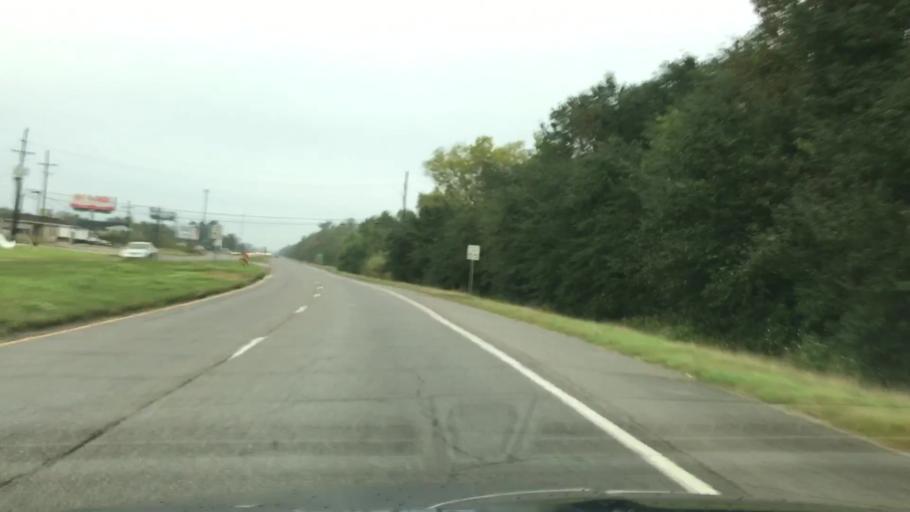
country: US
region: Louisiana
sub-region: Saint Charles Parish
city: Des Allemands
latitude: 29.8206
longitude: -90.4837
